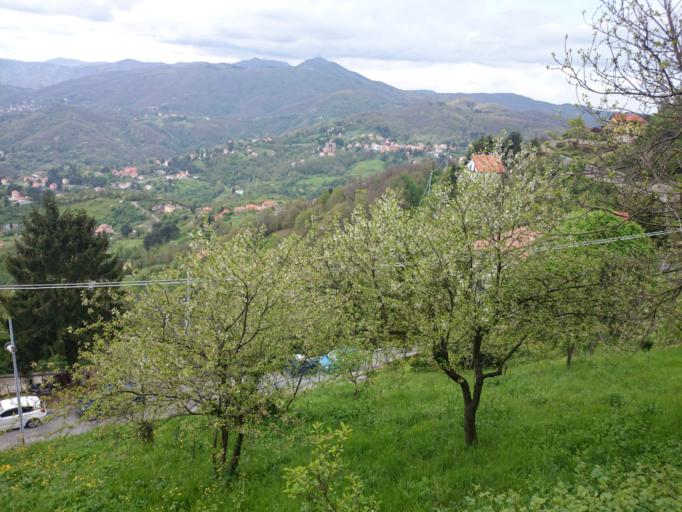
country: IT
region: Liguria
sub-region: Provincia di Genova
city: Busalla
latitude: 44.5452
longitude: 8.9555
